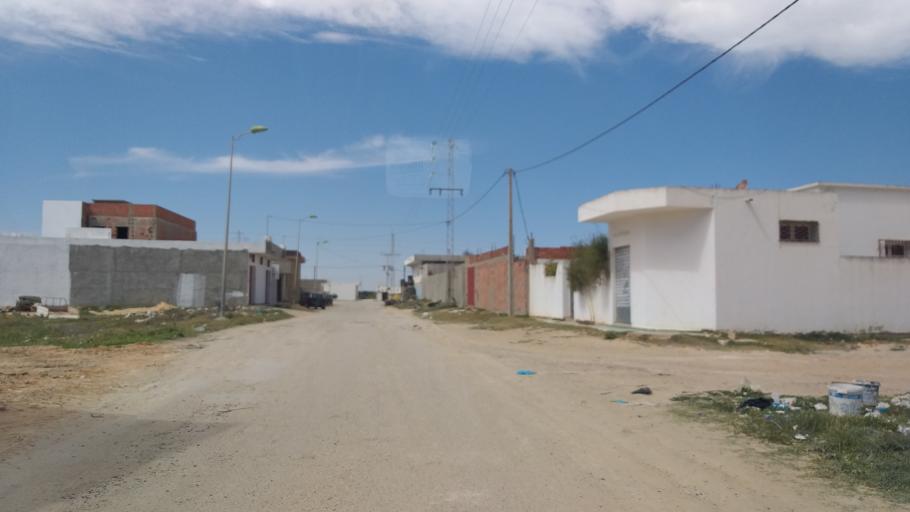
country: TN
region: Al Mahdiyah
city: El Jem
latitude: 35.3051
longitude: 10.6931
